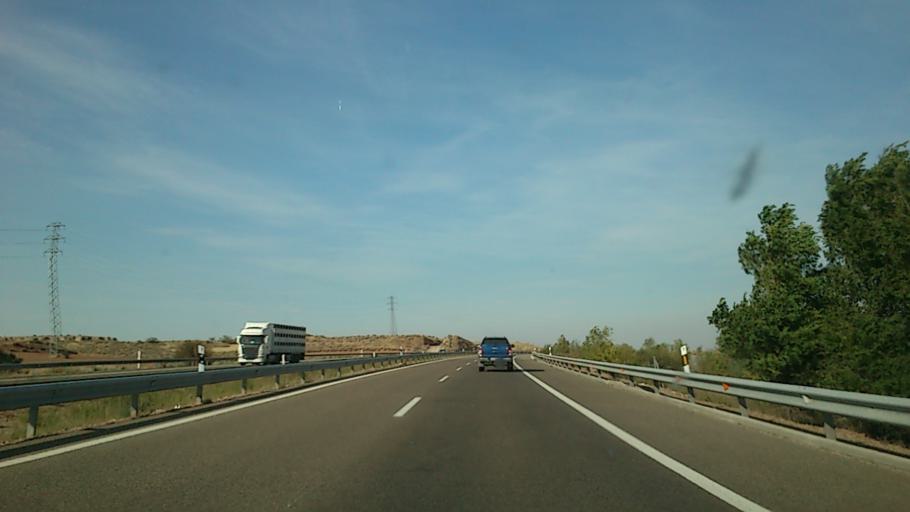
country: ES
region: Aragon
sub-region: Provincia de Zaragoza
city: Longares
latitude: 41.4442
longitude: -1.1397
